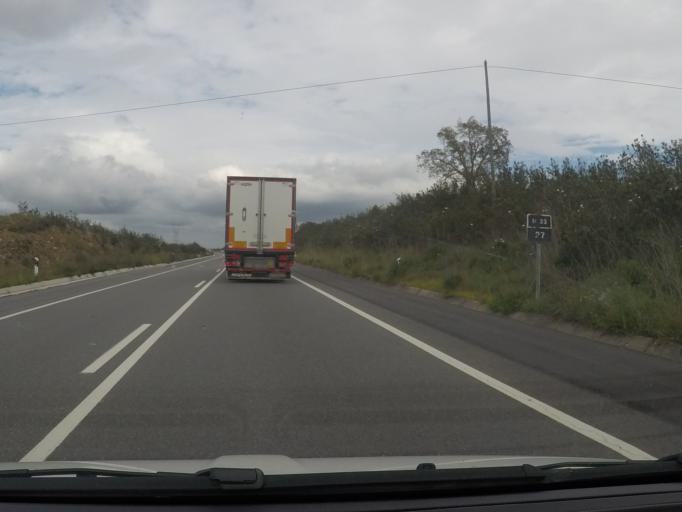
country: PT
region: Setubal
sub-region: Santiago do Cacem
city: Santiago do Cacem
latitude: 38.0709
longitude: -8.6624
